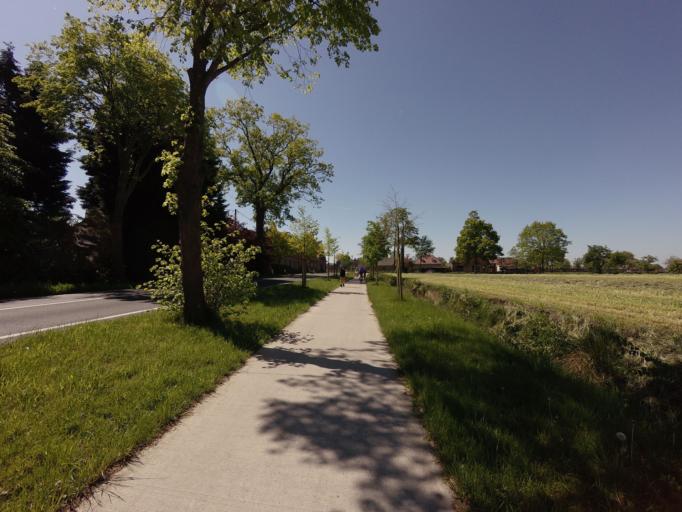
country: BE
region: Flanders
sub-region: Provincie Antwerpen
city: Essen
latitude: 51.4510
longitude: 4.4278
